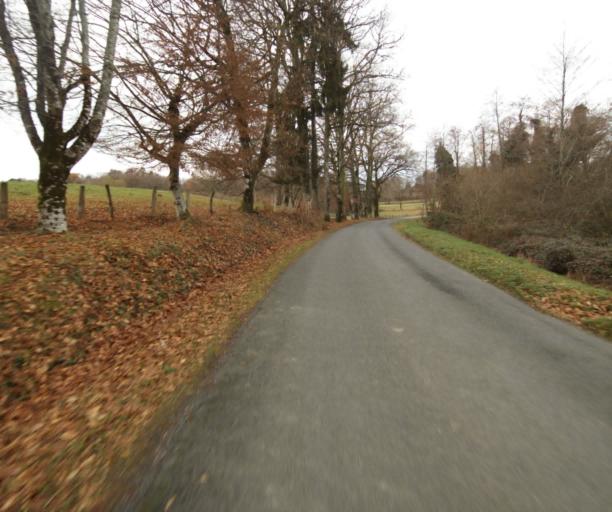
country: FR
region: Limousin
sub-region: Departement de la Correze
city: Chameyrat
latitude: 45.2495
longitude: 1.6833
